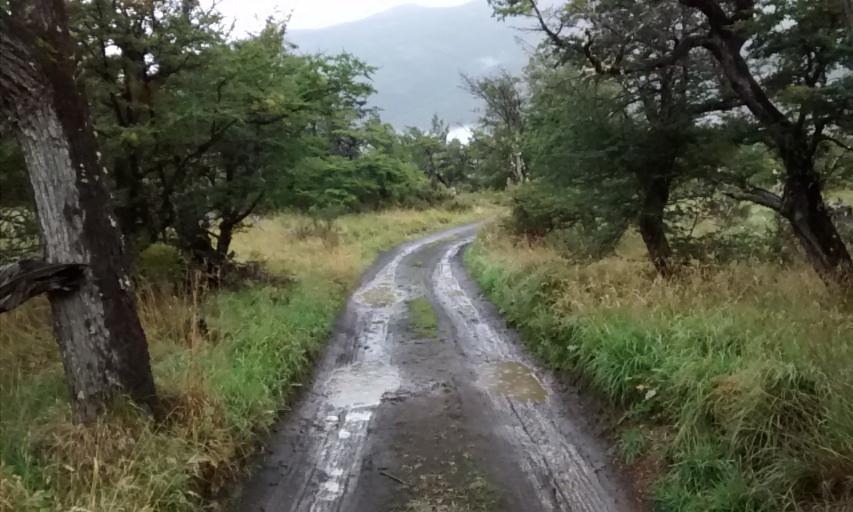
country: CL
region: Magallanes
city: Puerto Natales
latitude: -51.1233
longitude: -73.1135
